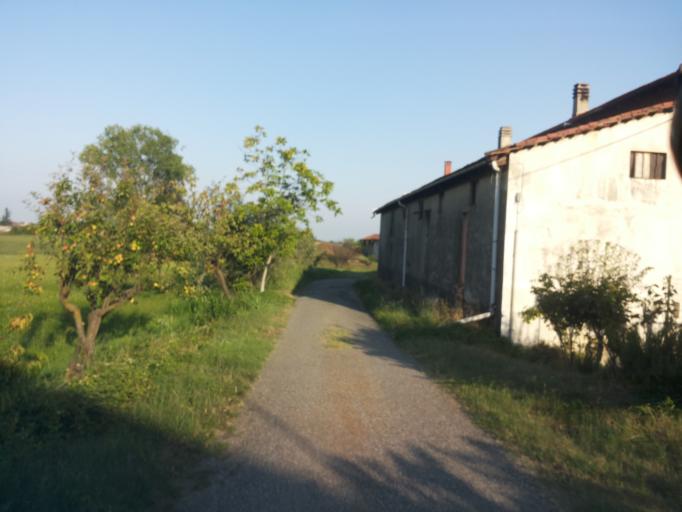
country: IT
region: Piedmont
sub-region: Provincia di Biella
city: Cavaglia
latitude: 45.3963
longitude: 8.1096
